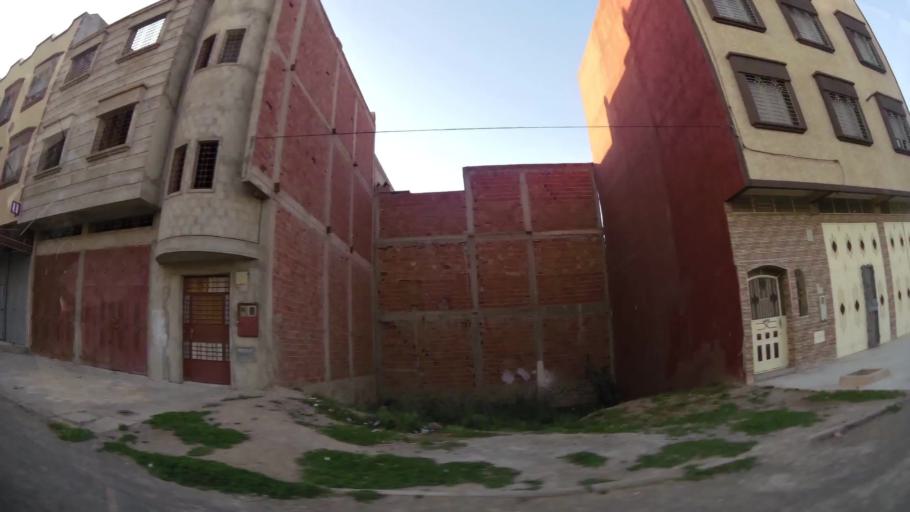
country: MA
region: Oriental
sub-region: Oujda-Angad
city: Oujda
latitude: 34.7143
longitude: -1.9064
